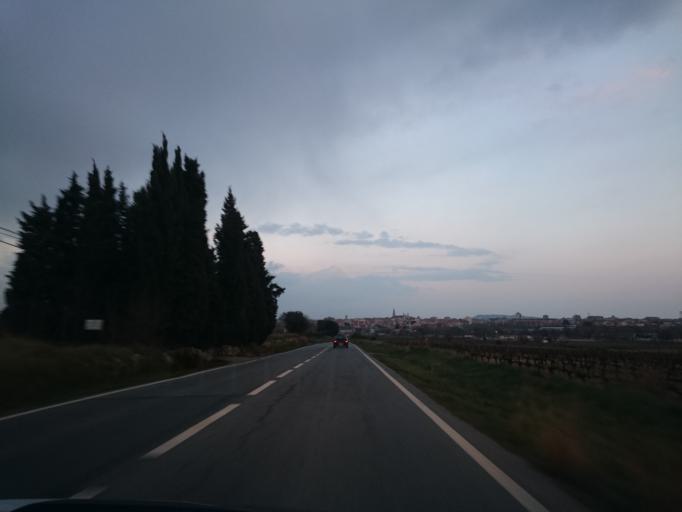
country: ES
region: Catalonia
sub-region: Provincia de Barcelona
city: Vilafranca del Penedes
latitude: 41.3522
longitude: 1.6789
